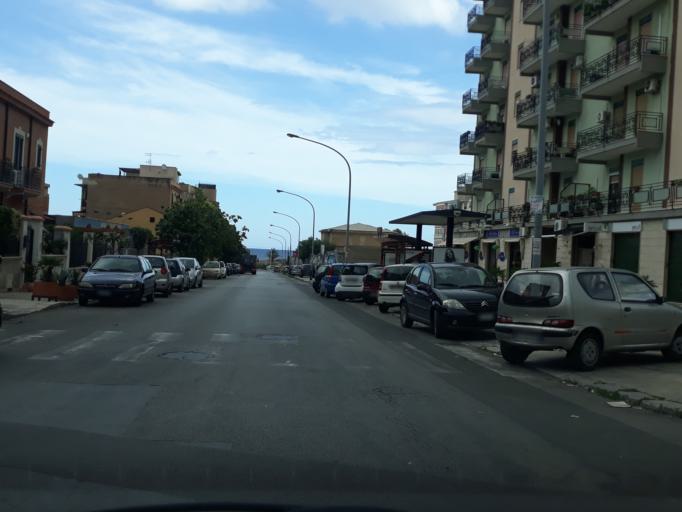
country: IT
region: Sicily
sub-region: Palermo
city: Ciaculli
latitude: 38.1011
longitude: 13.3936
